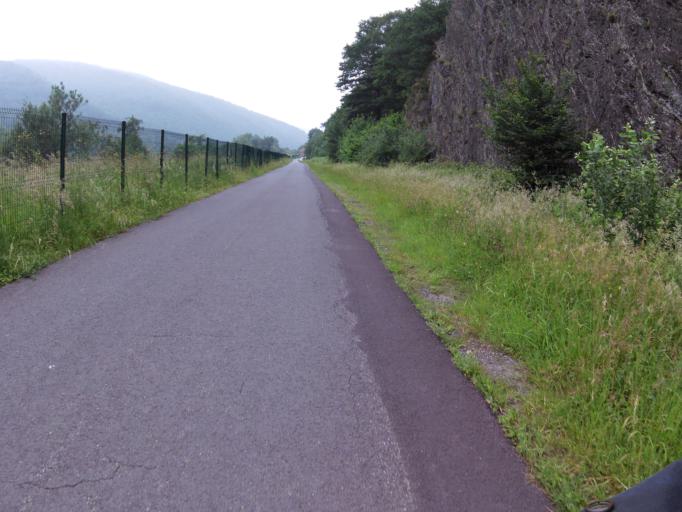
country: FR
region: Champagne-Ardenne
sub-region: Departement des Ardennes
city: Revin
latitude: 49.9503
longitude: 4.6545
